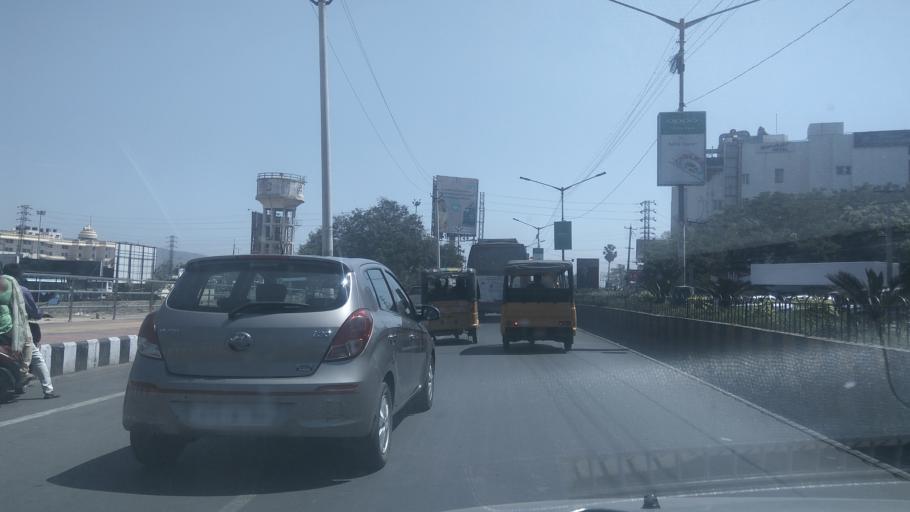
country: IN
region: Andhra Pradesh
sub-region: Chittoor
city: Tirupati
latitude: 13.6289
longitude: 79.4268
